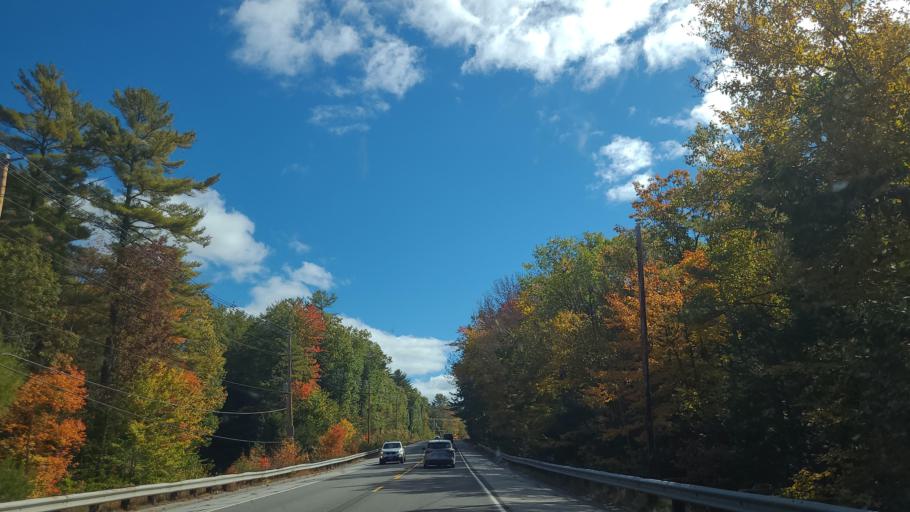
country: US
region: Maine
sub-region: Cumberland County
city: Bridgton
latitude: 43.9853
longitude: -70.6395
